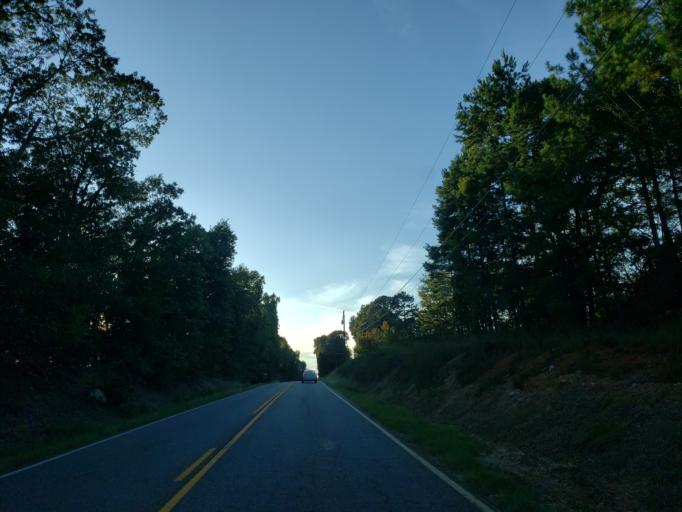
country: US
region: Georgia
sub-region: Bartow County
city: Euharlee
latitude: 34.2395
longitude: -84.9981
